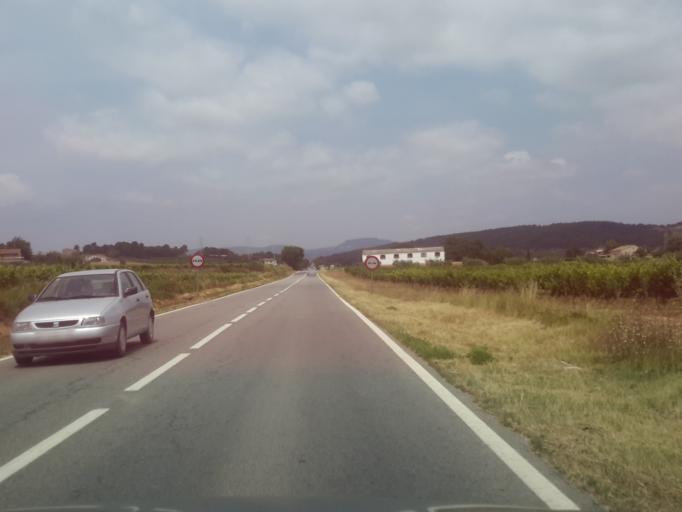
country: ES
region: Catalonia
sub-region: Provincia de Barcelona
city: Vilobi del Penedes
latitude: 41.3666
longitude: 1.6552
